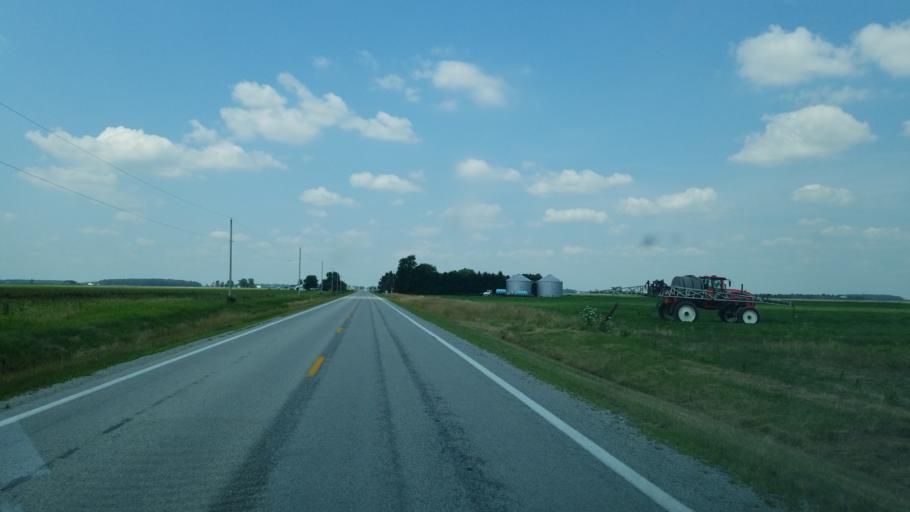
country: US
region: Ohio
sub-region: Henry County
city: Deshler
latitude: 41.2836
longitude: -83.9648
